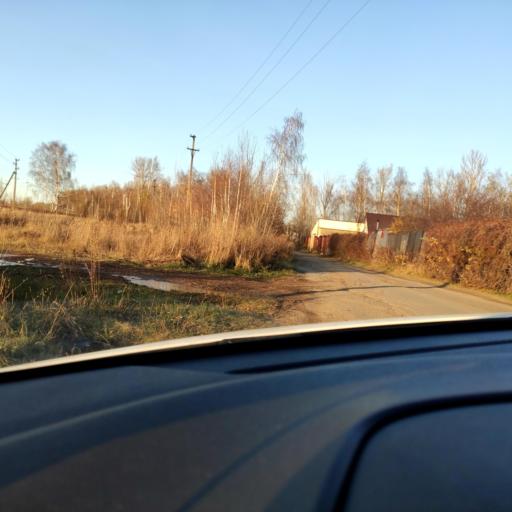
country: RU
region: Tatarstan
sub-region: Gorod Kazan'
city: Kazan
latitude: 55.9049
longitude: 49.0651
